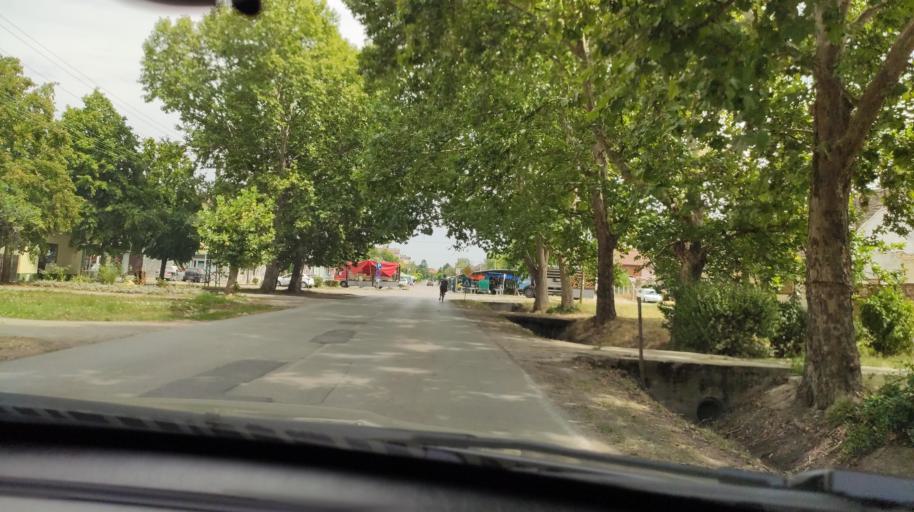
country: RS
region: Autonomna Pokrajina Vojvodina
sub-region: Juznobacki Okrug
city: Temerin
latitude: 45.4084
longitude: 19.8830
